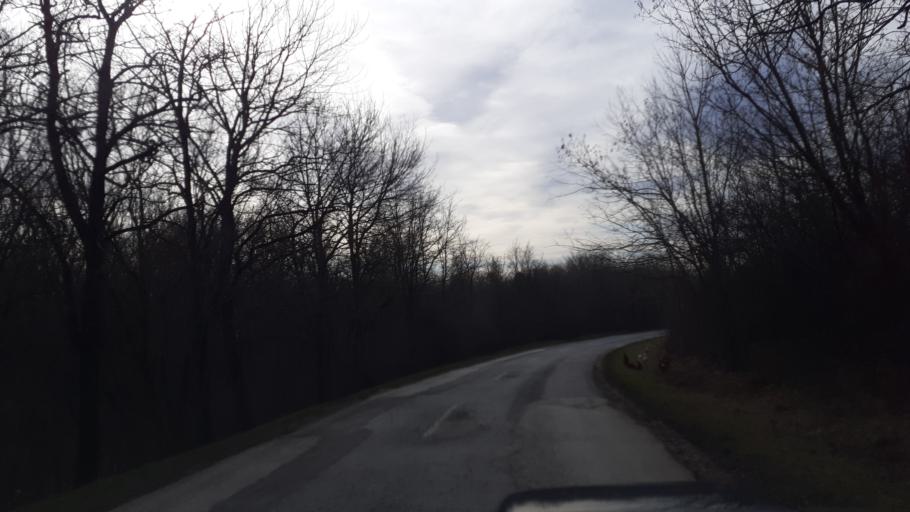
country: HU
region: Fejer
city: Sarbogard
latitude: 46.9116
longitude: 18.6653
